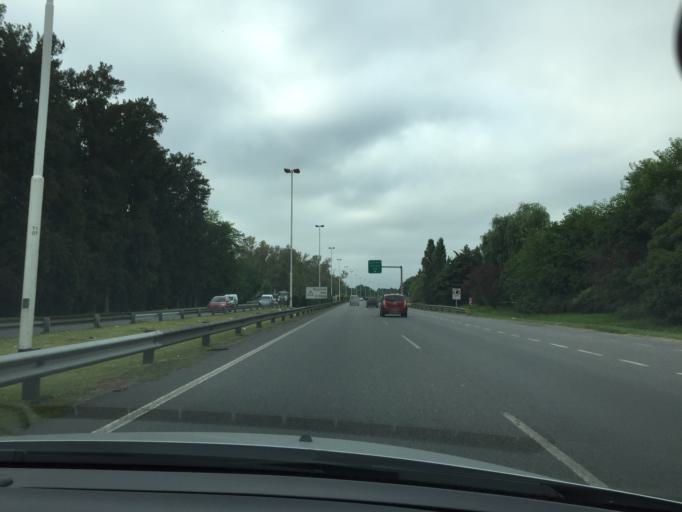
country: AR
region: Buenos Aires
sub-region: Partido de Ezeiza
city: Ezeiza
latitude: -34.7876
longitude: -58.5199
